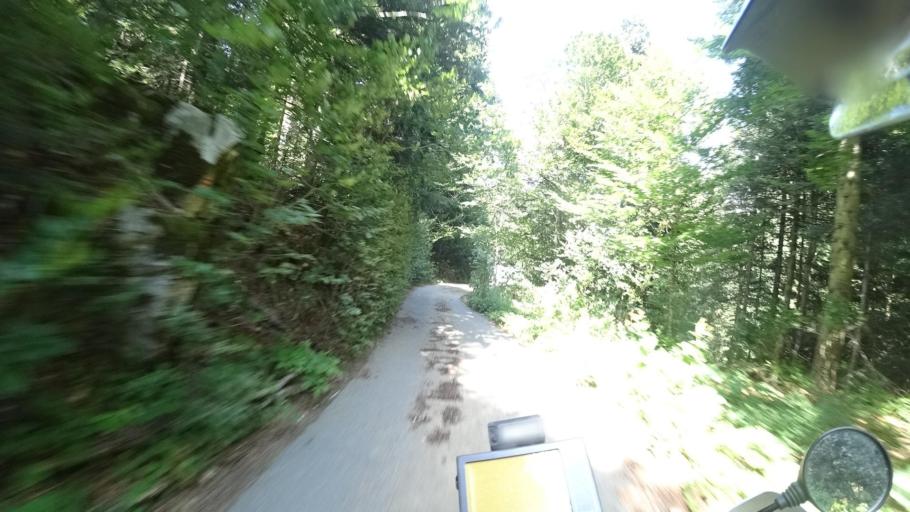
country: HR
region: Licko-Senjska
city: Brinje
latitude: 45.1237
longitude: 15.0399
